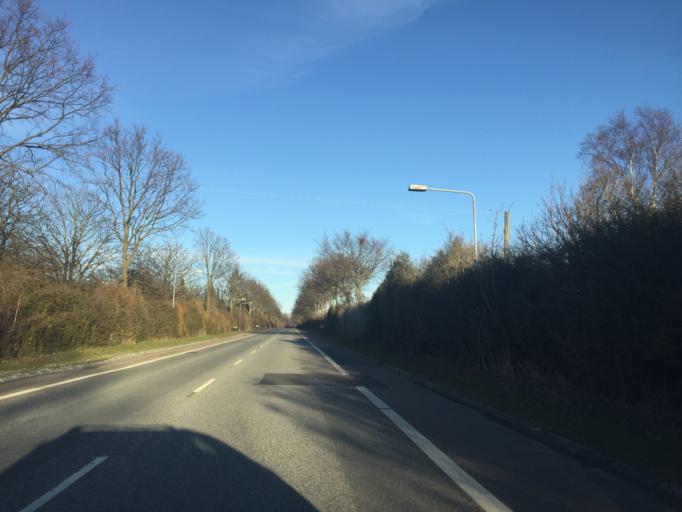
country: DK
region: Capital Region
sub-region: Dragor Kommune
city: Dragor
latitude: 55.5897
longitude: 12.6442
